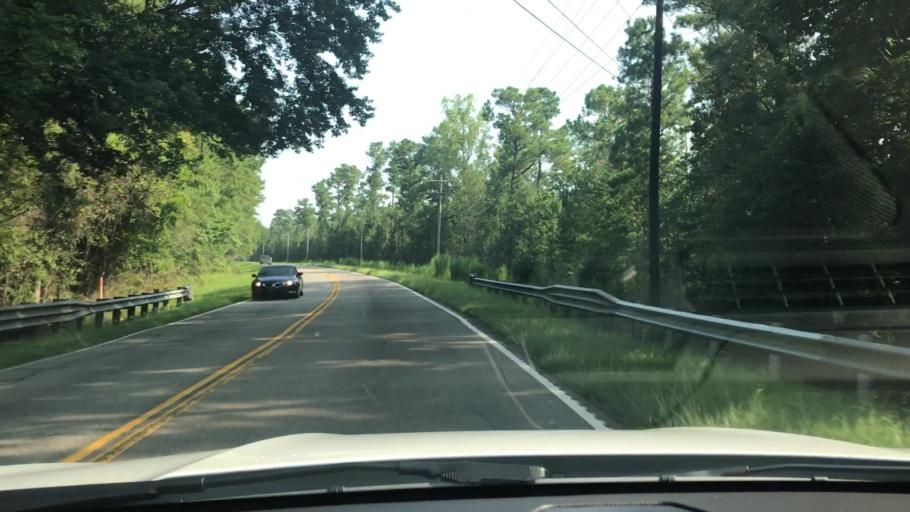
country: US
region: South Carolina
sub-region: Georgetown County
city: Georgetown
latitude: 33.4376
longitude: -79.2762
